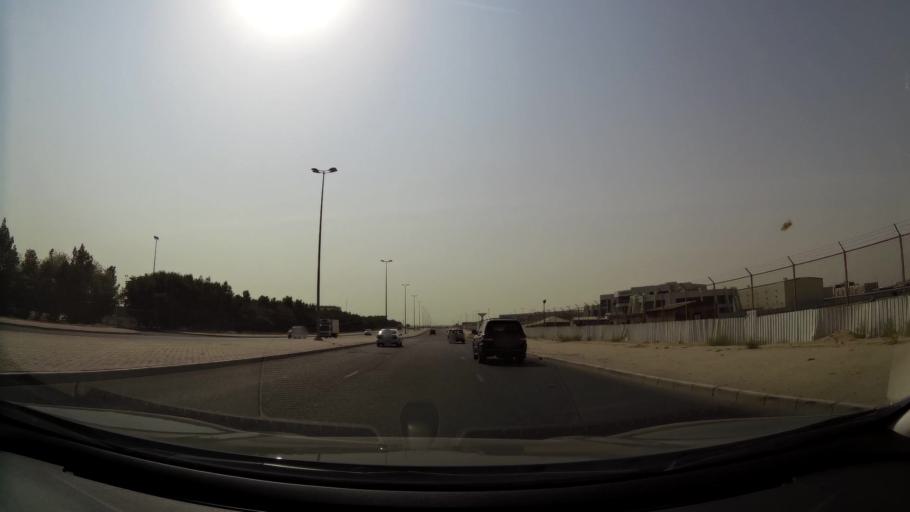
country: KW
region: Al Asimah
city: Ar Rabiyah
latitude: 29.2865
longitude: 47.9143
